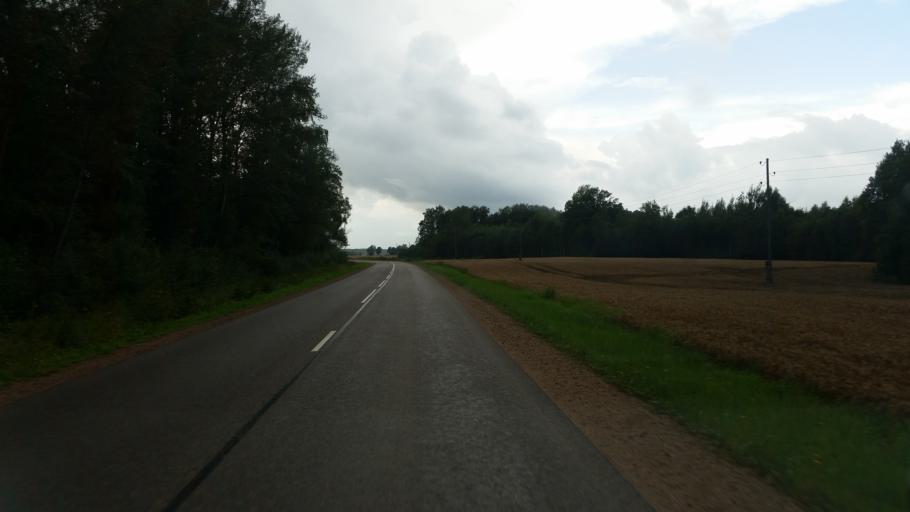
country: LV
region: Vecumnieki
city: Vecumnieki
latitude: 56.4326
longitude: 24.4423
